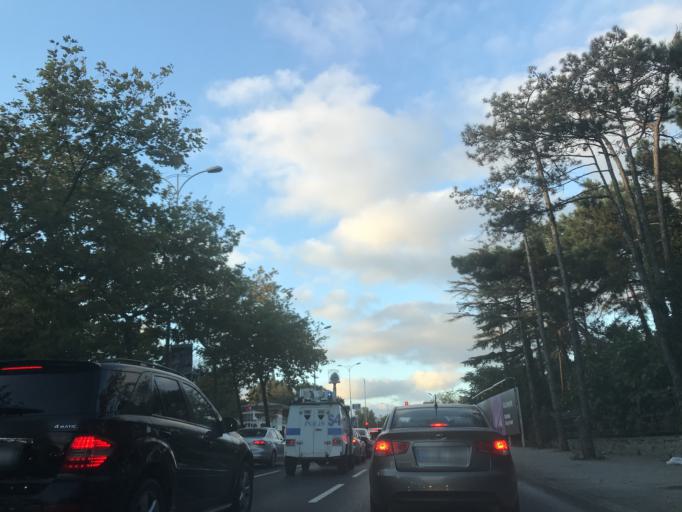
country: TR
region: Istanbul
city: Sisli
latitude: 41.1338
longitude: 29.0250
